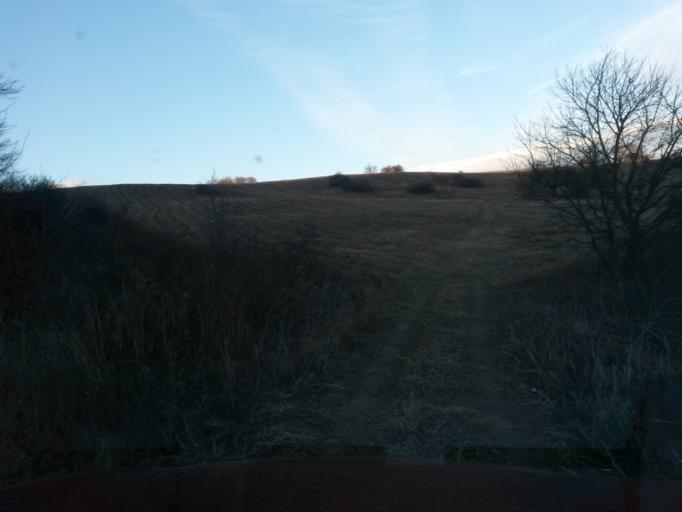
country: SK
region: Kosicky
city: Kosice
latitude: 48.7047
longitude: 21.3094
